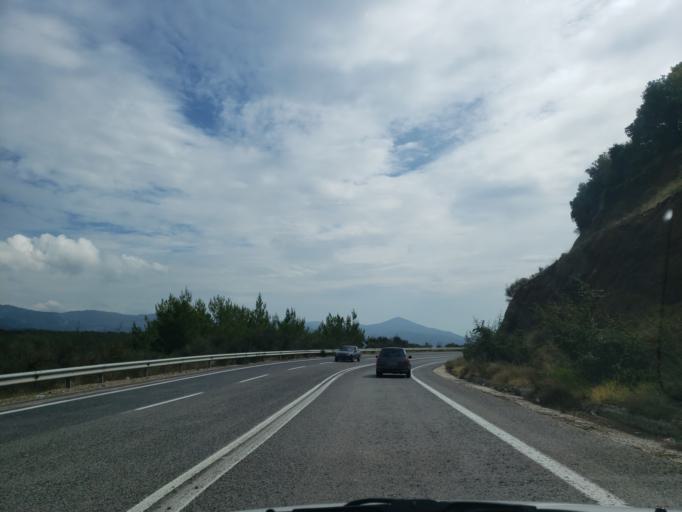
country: GR
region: Central Greece
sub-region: Nomos Fthiotidos
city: Stavros
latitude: 38.9775
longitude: 22.3807
